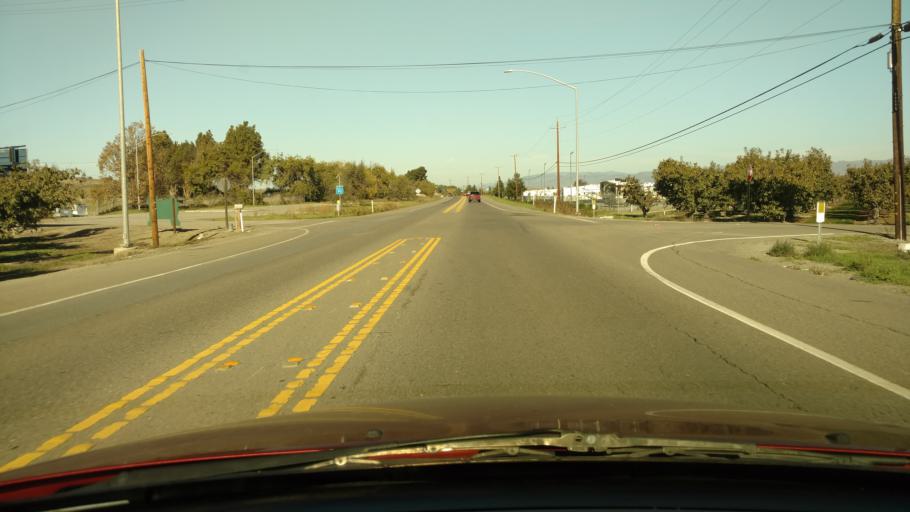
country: US
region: California
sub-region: San Benito County
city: Hollister
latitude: 36.8775
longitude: -121.4122
